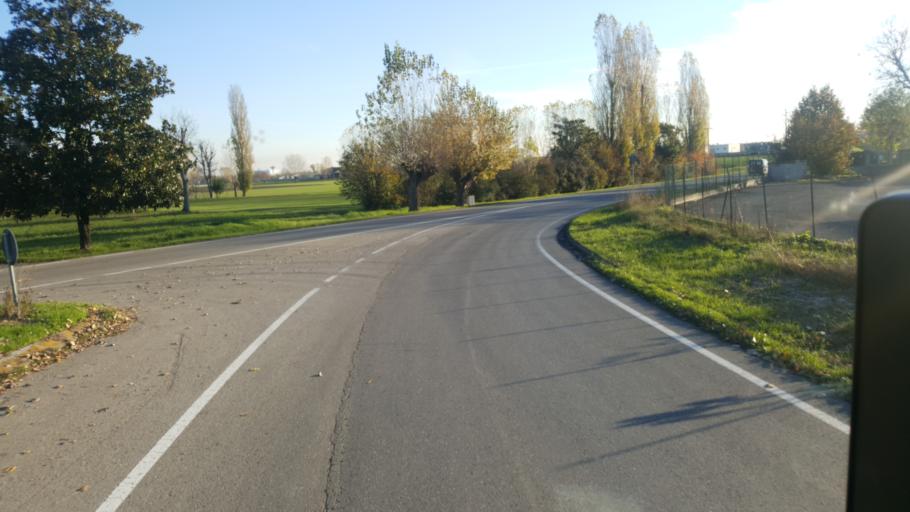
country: IT
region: Emilia-Romagna
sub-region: Provincia di Parma
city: Ponte Taro
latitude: 44.8379
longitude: 10.2097
